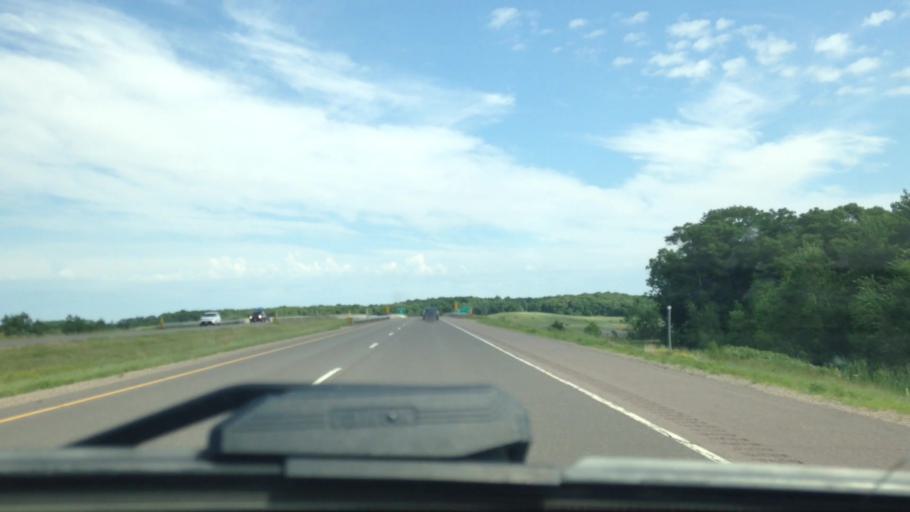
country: US
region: Wisconsin
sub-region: Washburn County
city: Spooner
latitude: 45.8495
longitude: -91.8601
